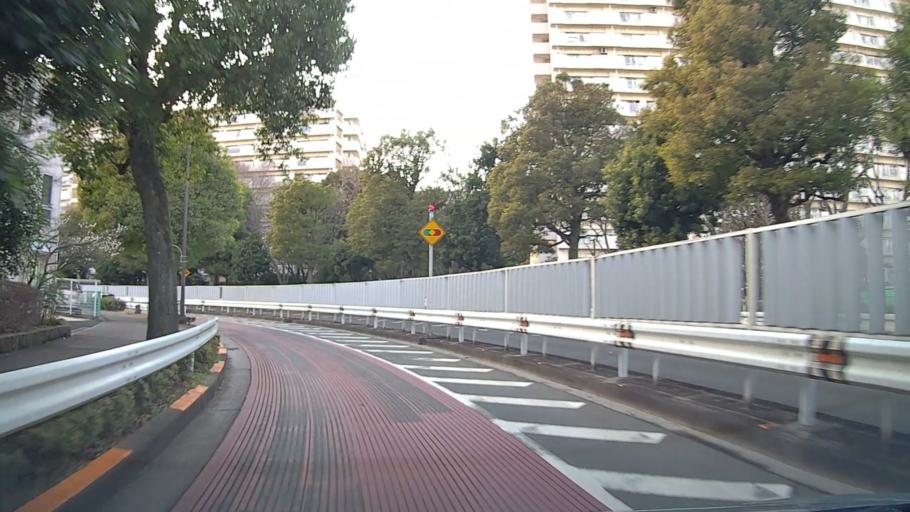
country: JP
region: Saitama
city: Wako
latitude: 35.7608
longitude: 139.6322
